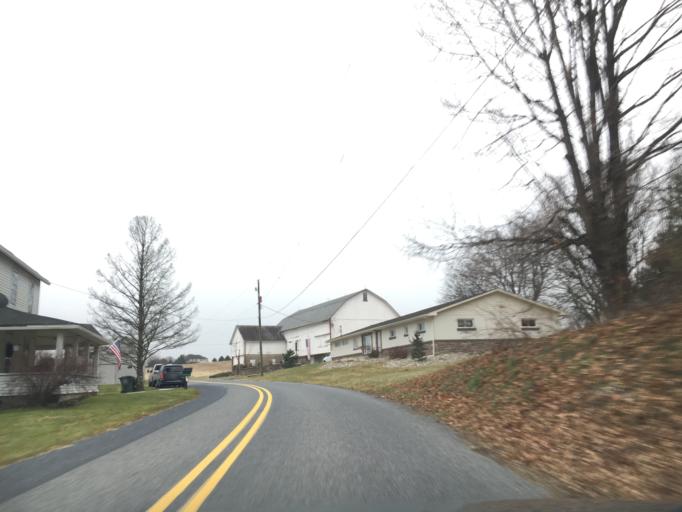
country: US
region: Pennsylvania
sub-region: Lehigh County
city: Schnecksville
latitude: 40.6924
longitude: -75.5839
